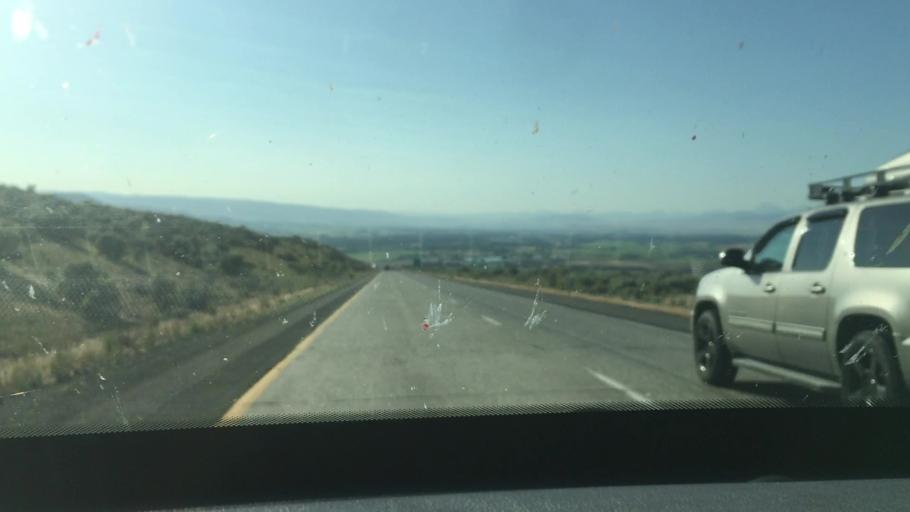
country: US
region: Washington
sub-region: Kittitas County
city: Kittitas
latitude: 46.9054
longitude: -120.4594
